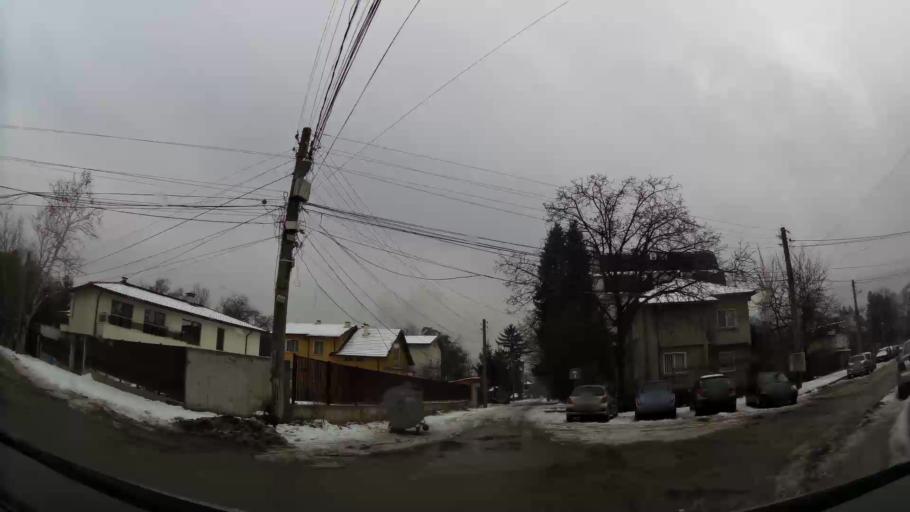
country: BG
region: Sofia-Capital
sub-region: Stolichna Obshtina
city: Sofia
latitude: 42.6752
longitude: 23.2669
